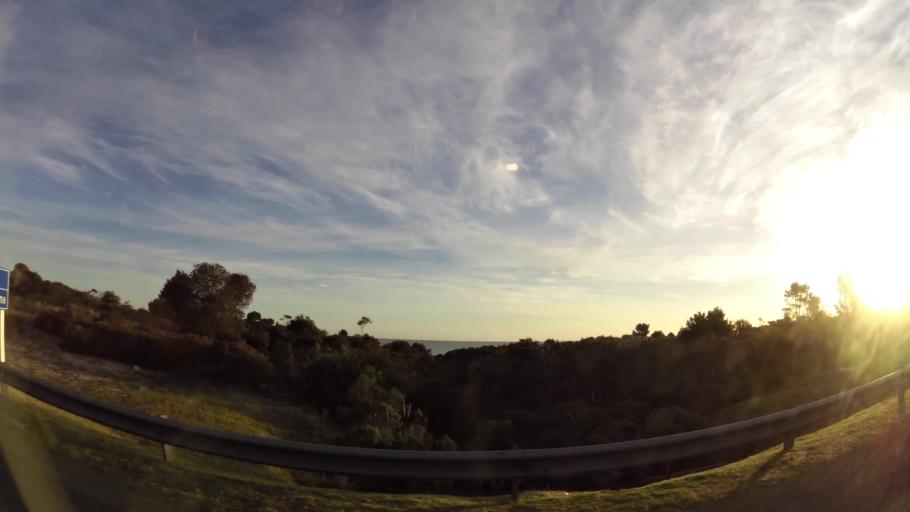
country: UY
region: Canelones
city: Atlantida
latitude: -34.7670
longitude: -55.7813
